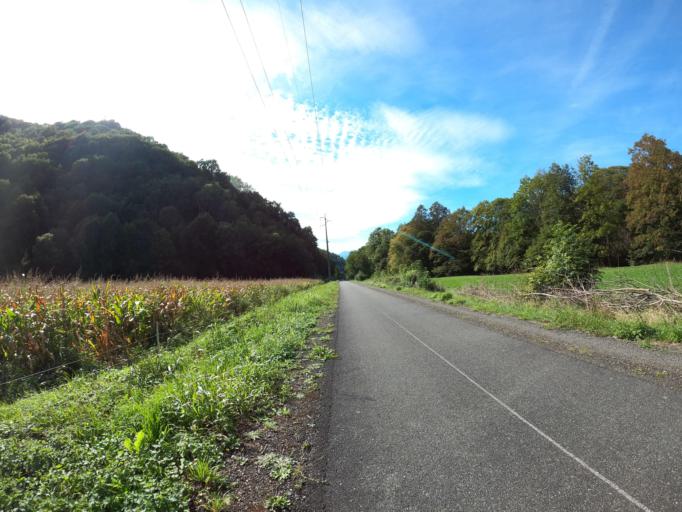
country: FR
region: Midi-Pyrenees
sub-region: Departement des Hautes-Pyrenees
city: Argeles-Gazost
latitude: 43.0362
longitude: -0.0610
